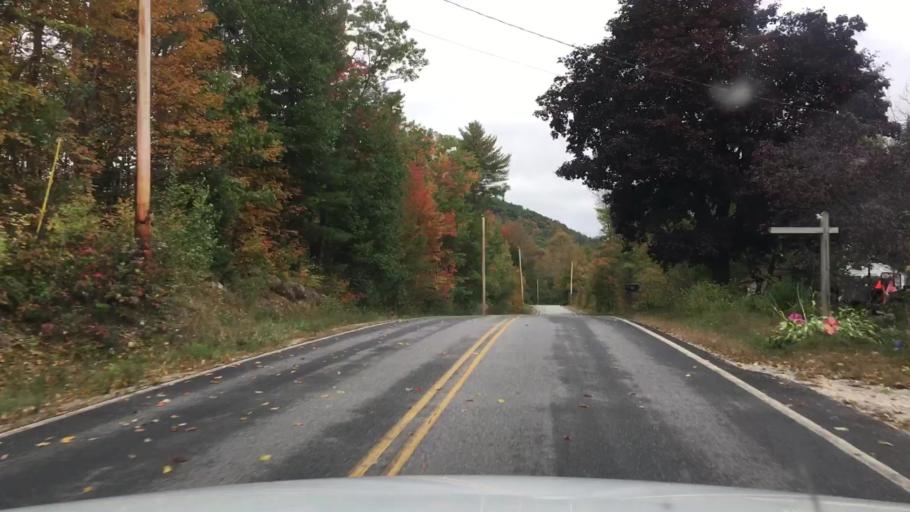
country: US
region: Maine
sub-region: Oxford County
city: Bethel
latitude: 44.2775
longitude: -70.7321
